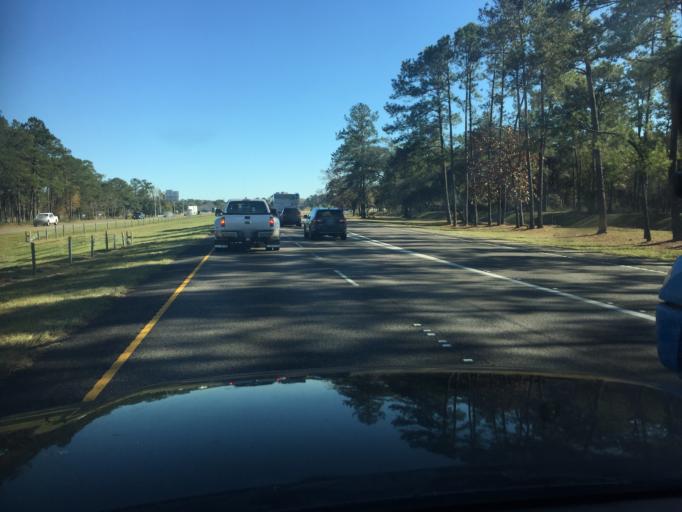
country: US
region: Louisiana
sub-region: Saint Tammany Parish
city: Covington
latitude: 30.4436
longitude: -90.1304
